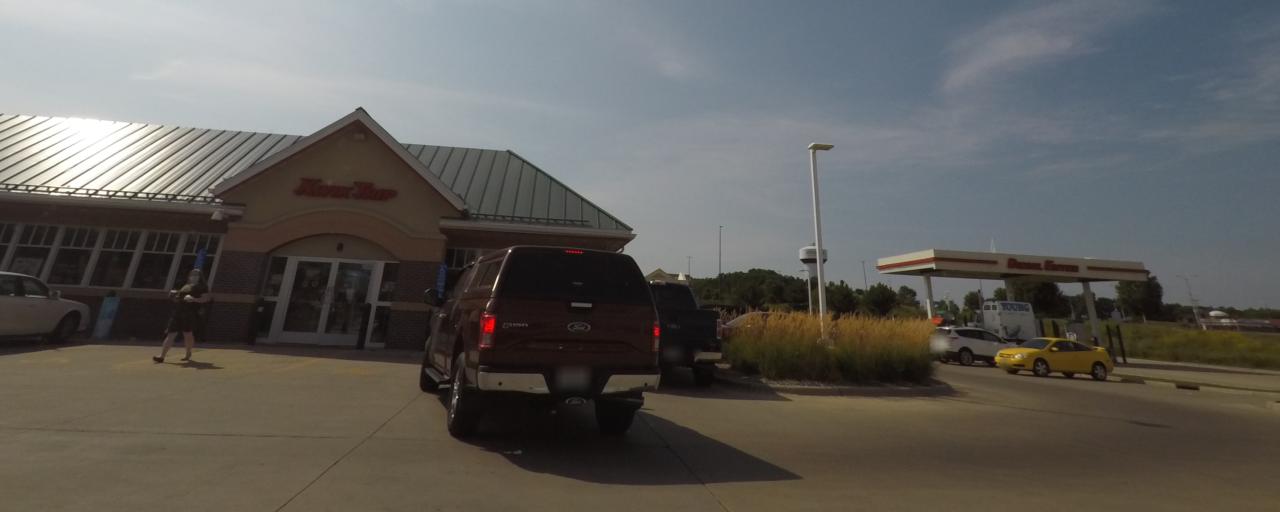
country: US
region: Wisconsin
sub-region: Jefferson County
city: Jefferson
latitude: 42.9903
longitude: -88.8077
